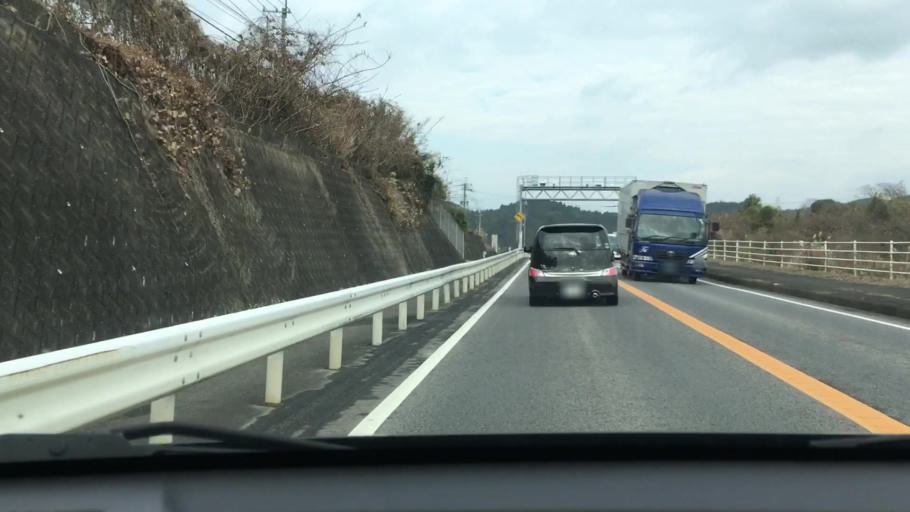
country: JP
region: Saga Prefecture
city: Imaricho-ko
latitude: 33.3308
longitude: 129.9304
